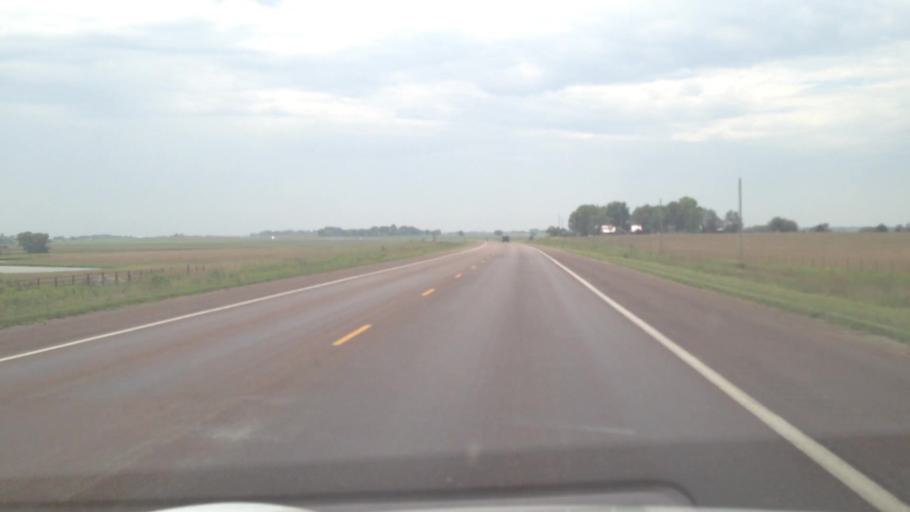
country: US
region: Kansas
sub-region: Crawford County
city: Girard
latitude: 37.4887
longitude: -94.8424
